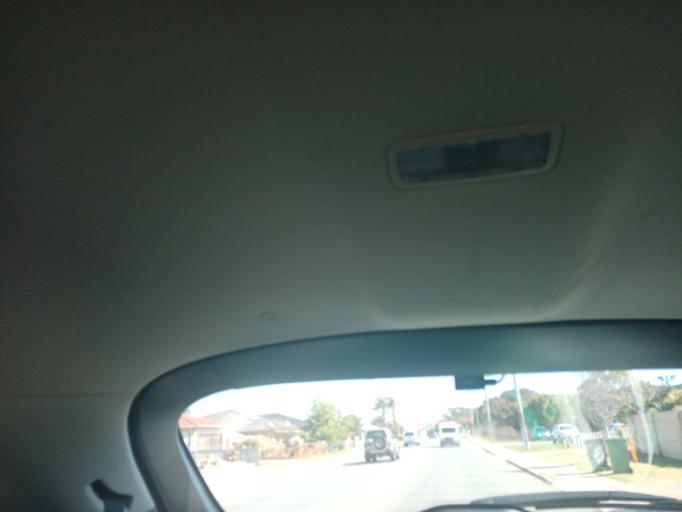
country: AU
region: Western Australia
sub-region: City of Cockburn
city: Spearwood
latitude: -32.1182
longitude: 115.7827
